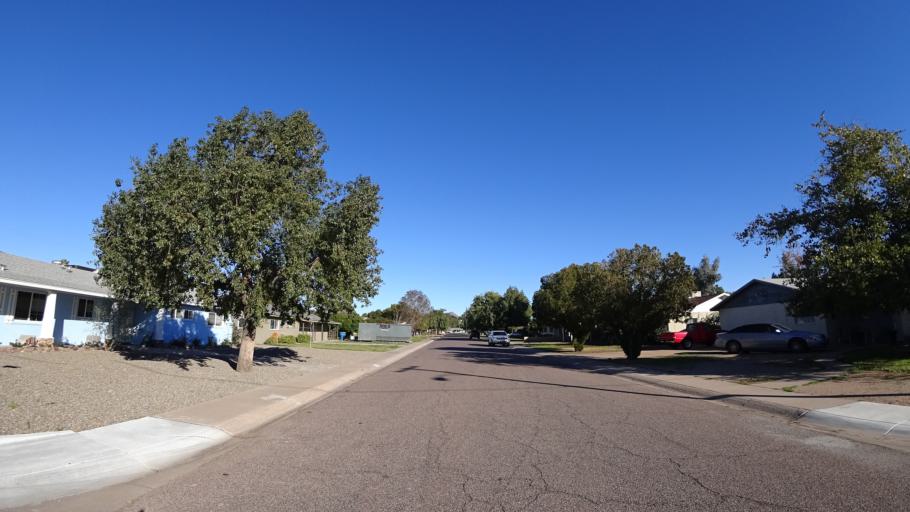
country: US
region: Arizona
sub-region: Maricopa County
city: Phoenix
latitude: 33.5146
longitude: -112.0540
